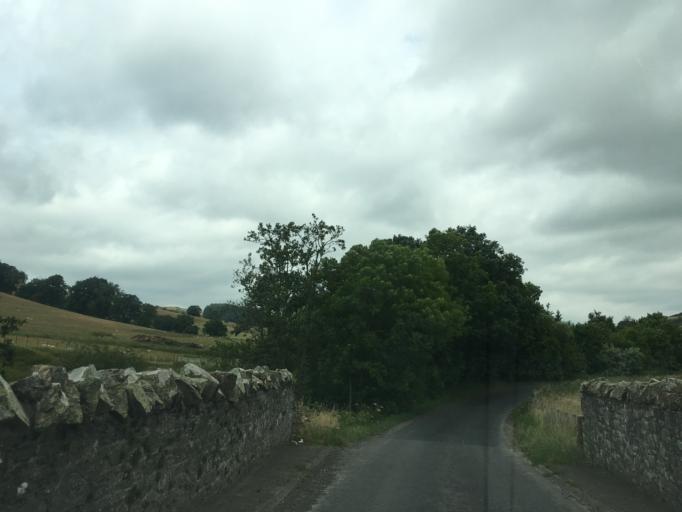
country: GB
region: Scotland
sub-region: The Scottish Borders
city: Peebles
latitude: 55.6715
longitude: -3.2056
